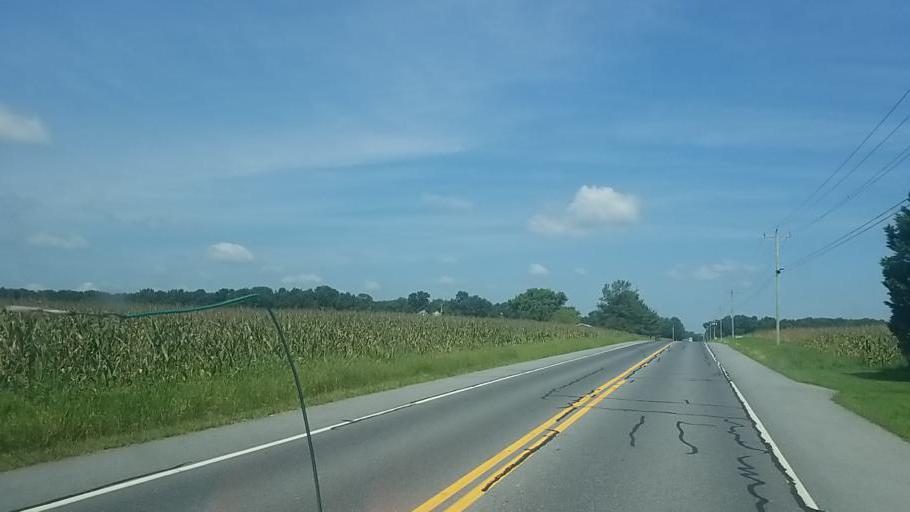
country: US
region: Delaware
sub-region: Sussex County
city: Seaford
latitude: 38.6761
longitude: -75.5780
